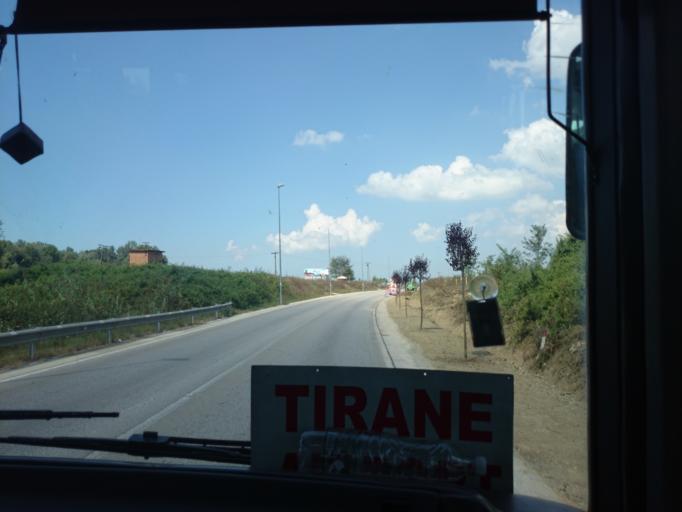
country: AL
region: Tirane
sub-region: Rrethi i Tiranes
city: Preze
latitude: 41.4134
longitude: 19.7028
